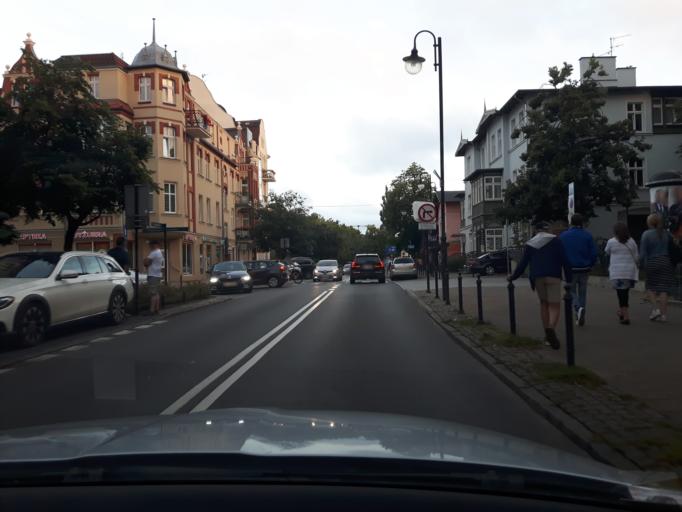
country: PL
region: Pomeranian Voivodeship
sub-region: Sopot
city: Sopot
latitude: 54.4422
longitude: 18.5635
